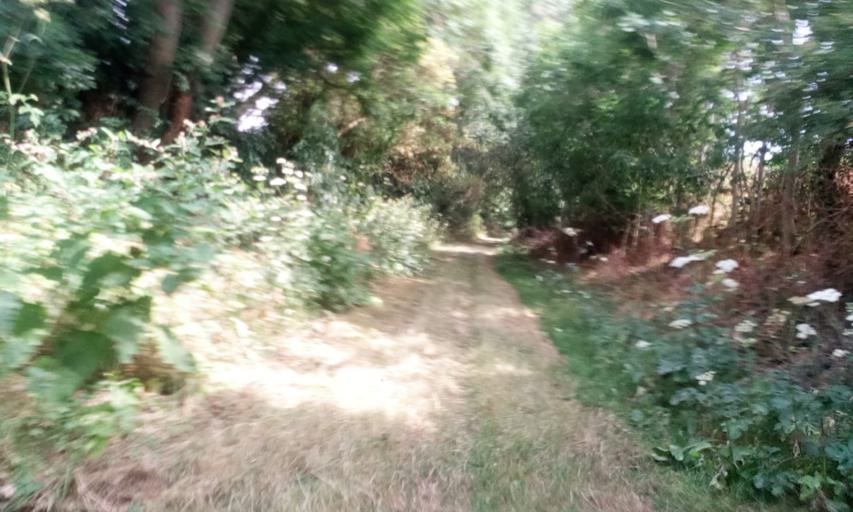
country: FR
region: Lower Normandy
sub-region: Departement du Calvados
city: Douvres-la-Delivrande
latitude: 49.2960
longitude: -0.4043
